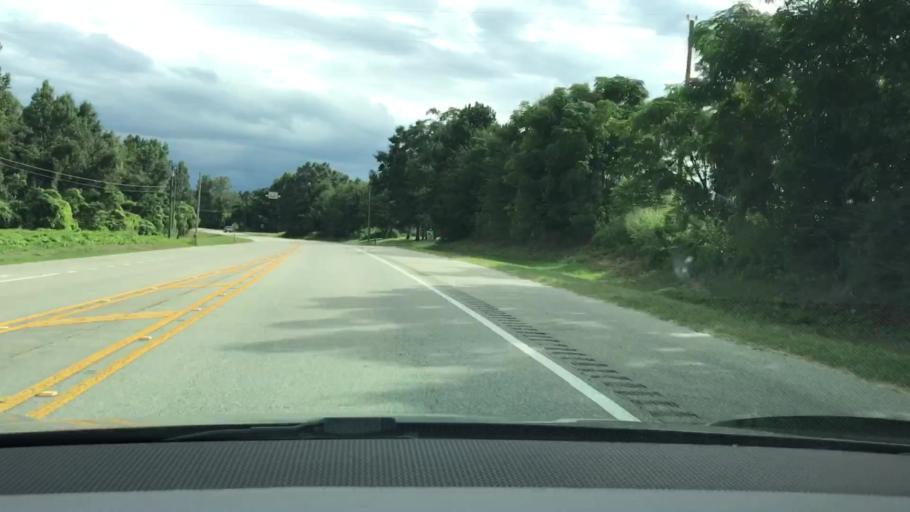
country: US
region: Alabama
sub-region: Coffee County
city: Elba
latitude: 31.5645
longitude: -86.0128
